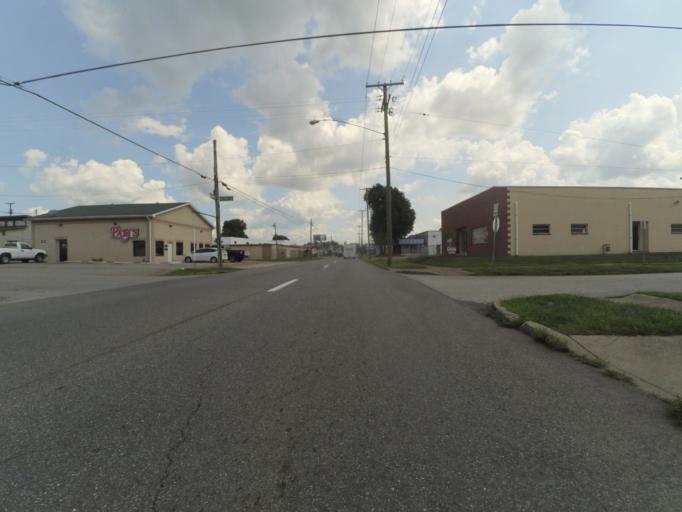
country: US
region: West Virginia
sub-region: Cabell County
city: Huntington
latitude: 38.4141
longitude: -82.4713
